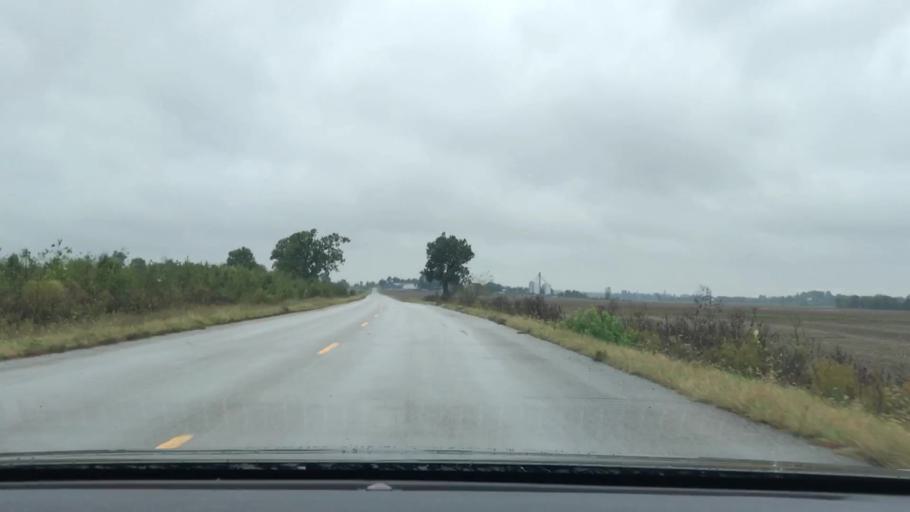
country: US
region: Kentucky
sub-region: Hopkins County
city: Madisonville
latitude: 37.3809
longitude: -87.3419
